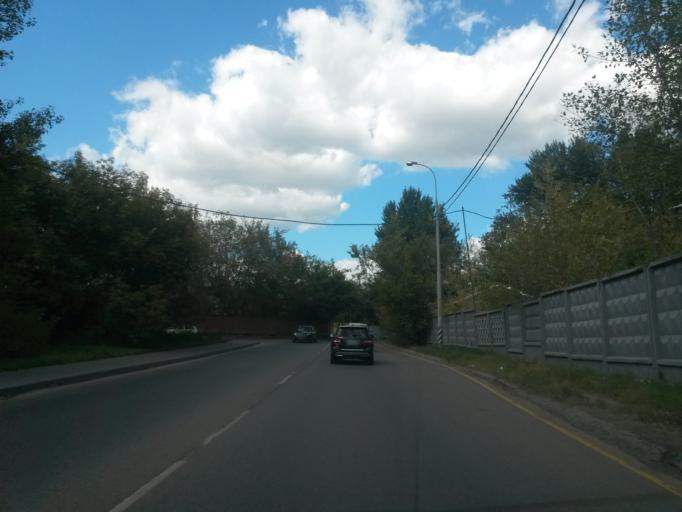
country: RU
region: Moscow
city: Tekstil'shchiki
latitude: 55.7002
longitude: 37.7071
